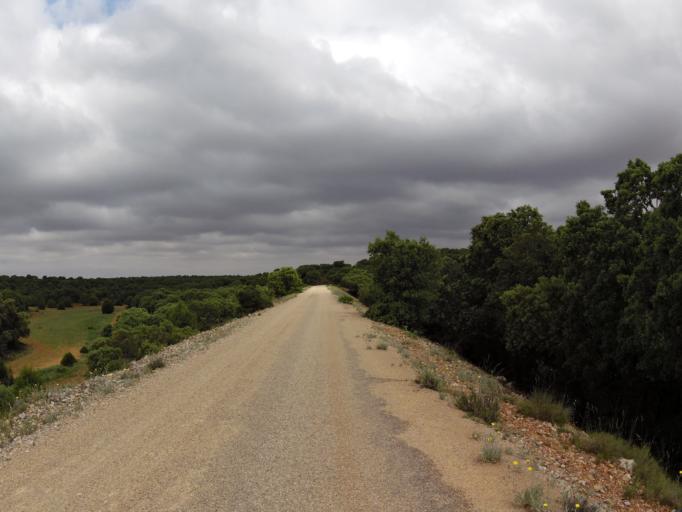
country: ES
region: Castille-La Mancha
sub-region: Provincia de Albacete
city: Robledo
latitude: 38.7458
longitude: -2.4706
